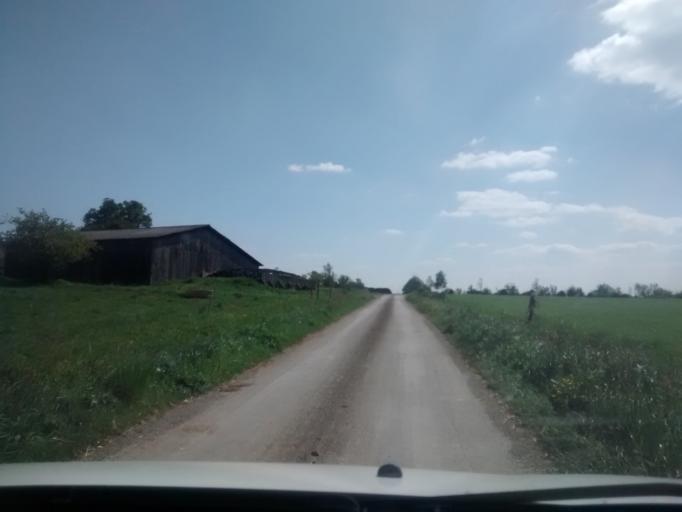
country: FR
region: Brittany
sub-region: Departement d'Ille-et-Vilaine
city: Fouillard
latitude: 48.1575
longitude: -1.6083
